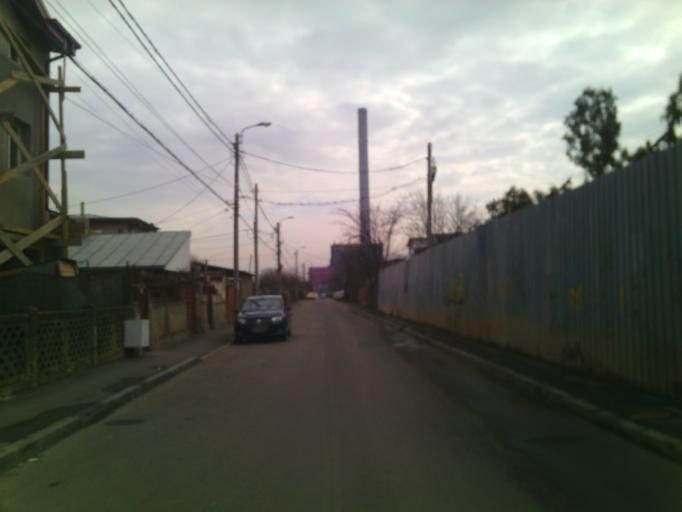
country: RO
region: Ilfov
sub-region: Comuna Jilava
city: Jilava
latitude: 44.3738
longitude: 26.0982
